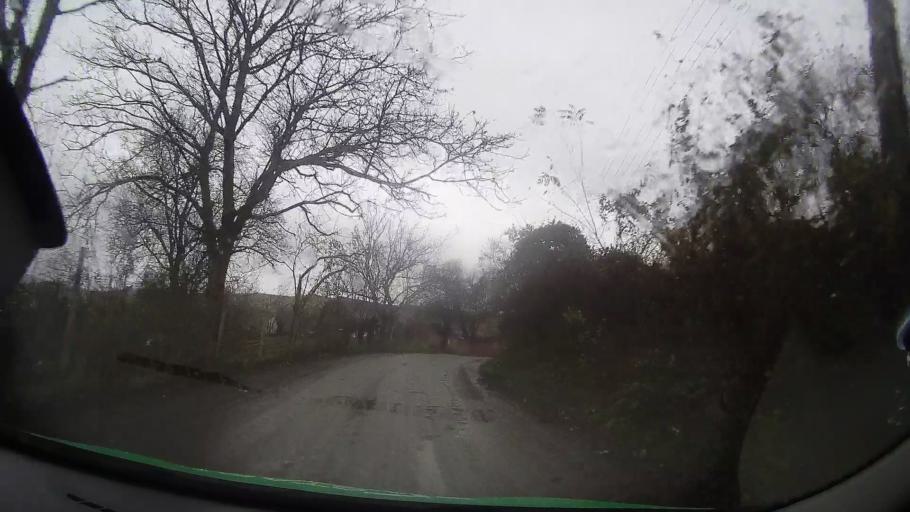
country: RO
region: Bistrita-Nasaud
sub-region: Comuna Monor
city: Monor
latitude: 46.9500
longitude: 24.7050
